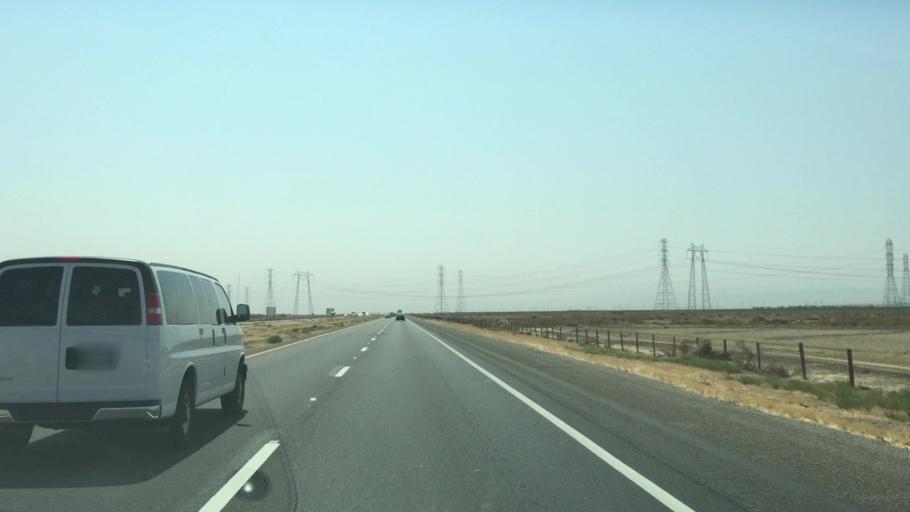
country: US
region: California
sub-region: Kern County
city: Buttonwillow
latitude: 35.3922
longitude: -119.3885
